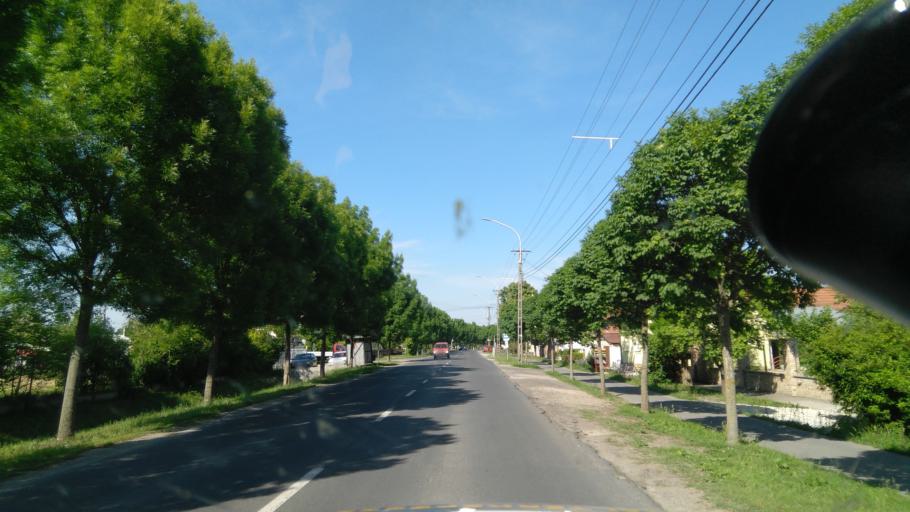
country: HU
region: Bekes
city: Gyula
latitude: 46.6563
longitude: 21.2854
